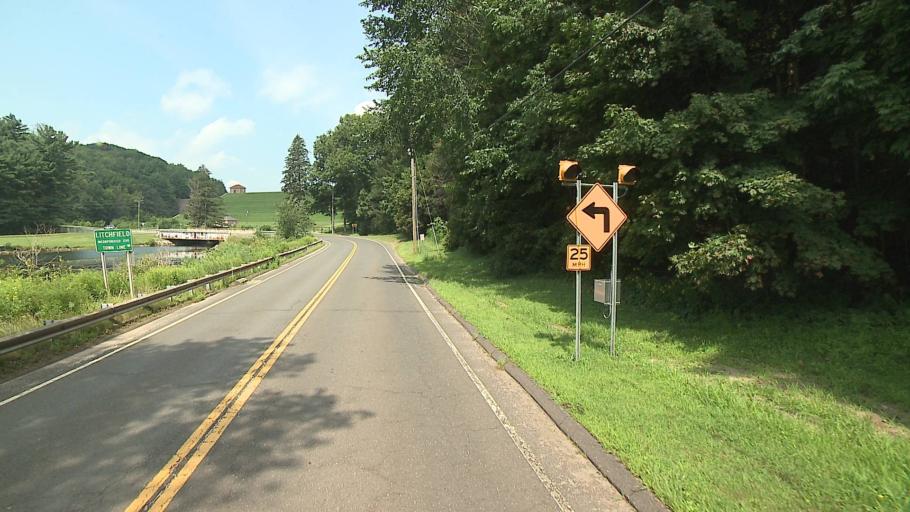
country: US
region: Connecticut
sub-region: Litchfield County
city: Thomaston
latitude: 41.6726
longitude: -73.1411
